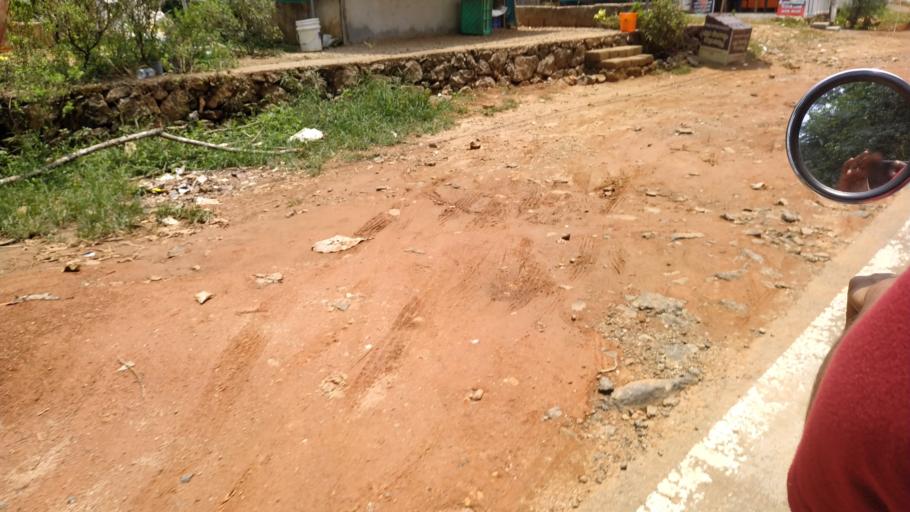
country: IN
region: Kerala
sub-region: Kottayam
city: Lalam
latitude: 9.8319
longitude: 76.7605
